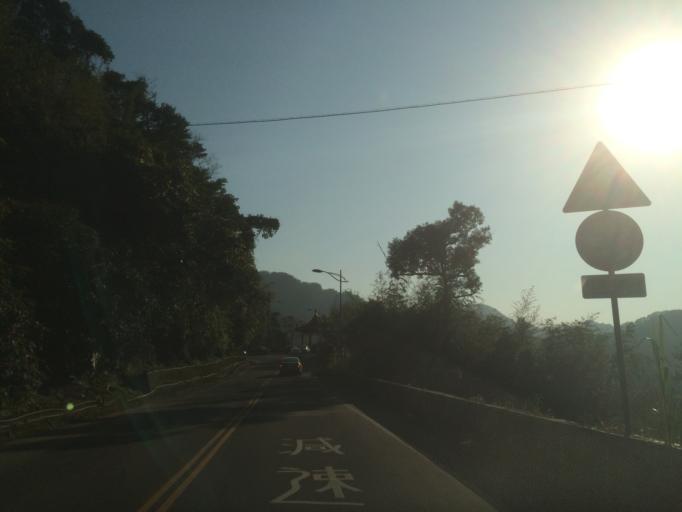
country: TW
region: Taiwan
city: Daxi
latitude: 24.8116
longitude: 121.2576
